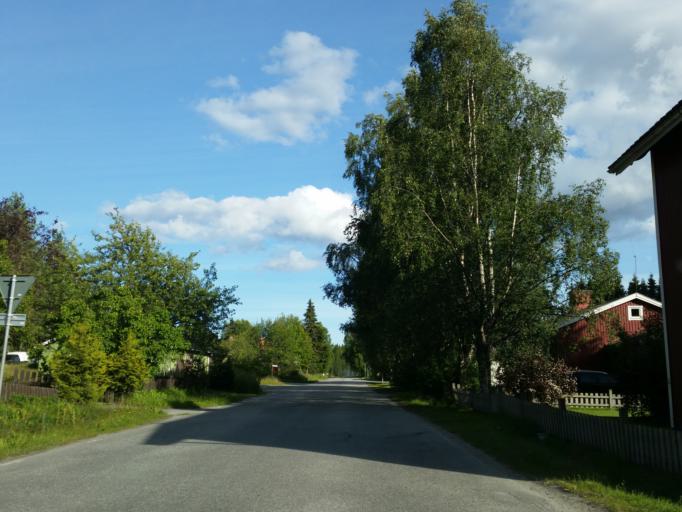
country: SE
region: Vaesterbotten
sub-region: Robertsfors Kommun
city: Robertsfors
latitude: 64.0603
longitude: 20.8507
